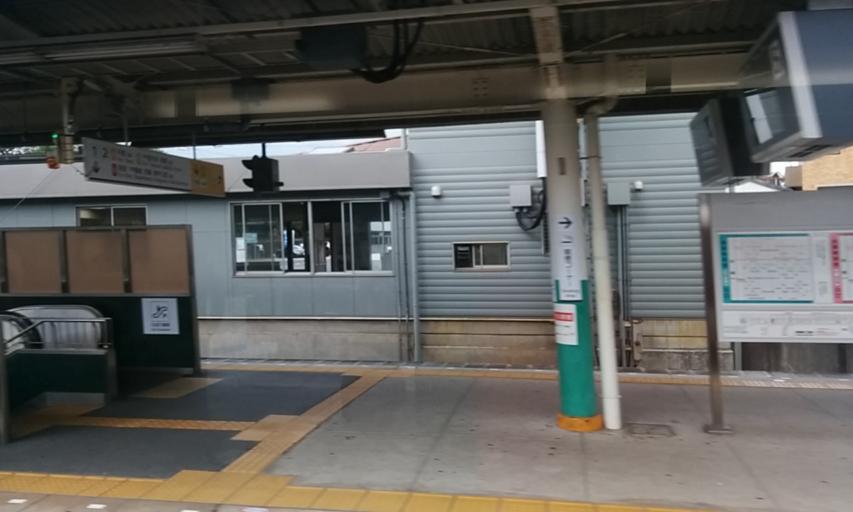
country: JP
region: Nara
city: Tawaramoto
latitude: 34.6067
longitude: 135.7827
